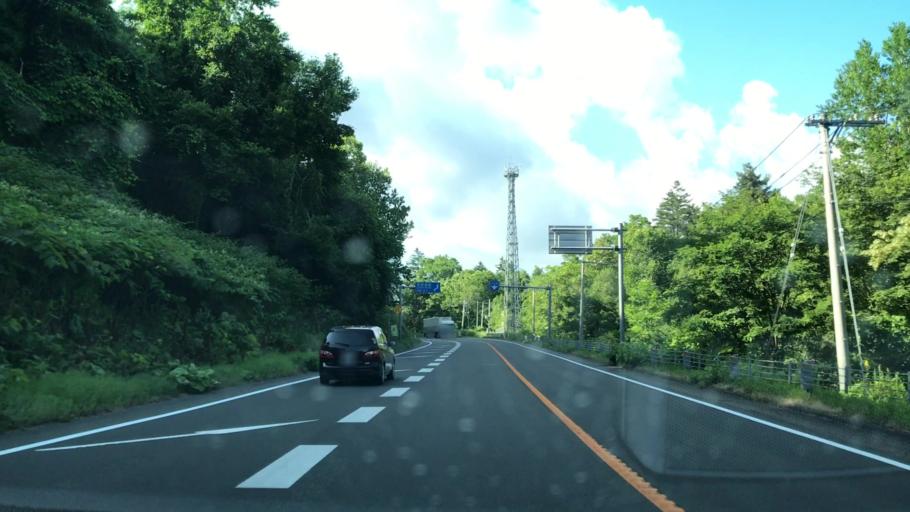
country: JP
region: Hokkaido
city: Shimo-furano
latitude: 42.9052
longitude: 142.4191
